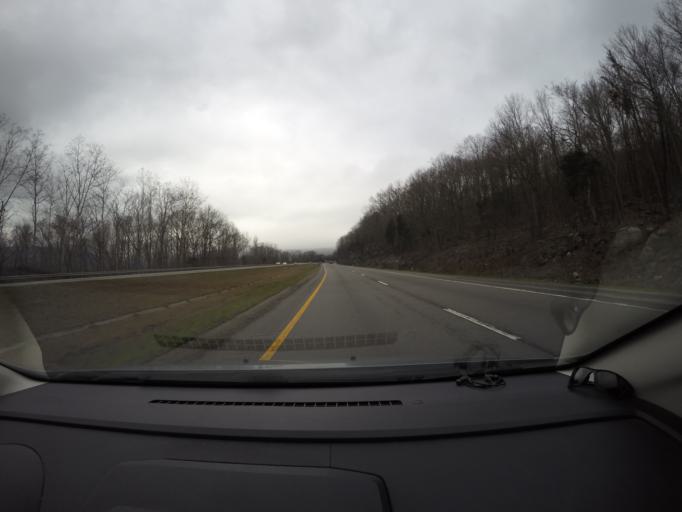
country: US
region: Tennessee
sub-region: Marion County
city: Monteagle
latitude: 35.2684
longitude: -85.8878
